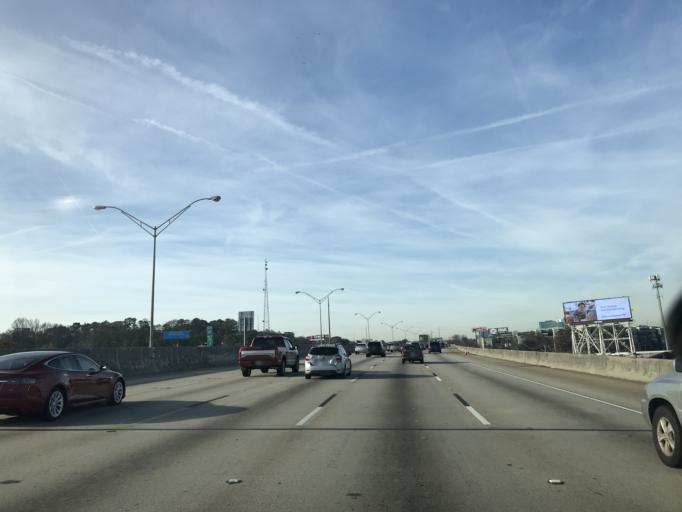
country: US
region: Georgia
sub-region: DeKalb County
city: Druid Hills
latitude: 33.8131
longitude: -84.3682
